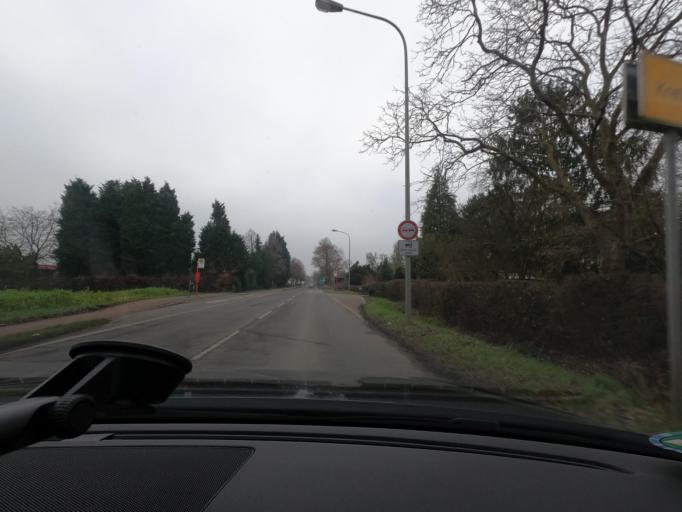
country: DE
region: North Rhine-Westphalia
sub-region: Regierungsbezirk Dusseldorf
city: Krefeld
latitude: 51.3714
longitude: 6.5645
